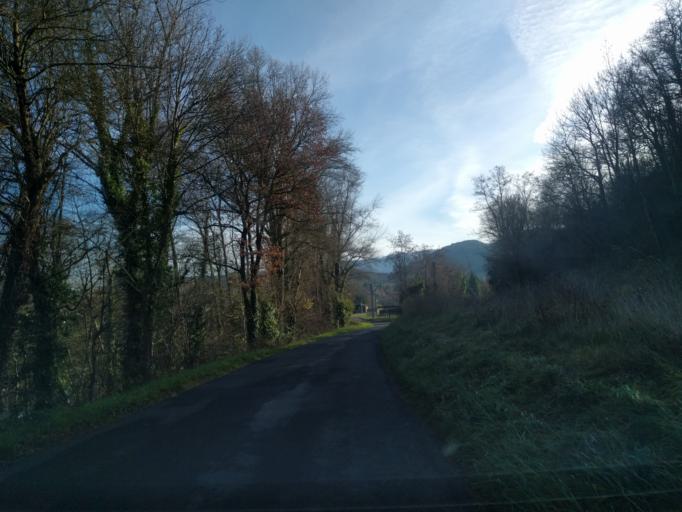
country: FR
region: Languedoc-Roussillon
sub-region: Departement de l'Aude
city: Quillan
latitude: 42.8947
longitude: 2.1902
